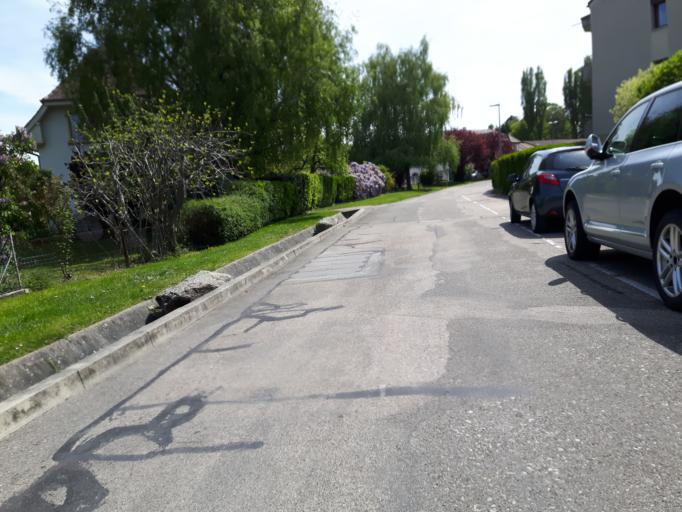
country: CH
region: Neuchatel
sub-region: Boudry District
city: Cortaillod
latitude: 46.9440
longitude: 6.8536
